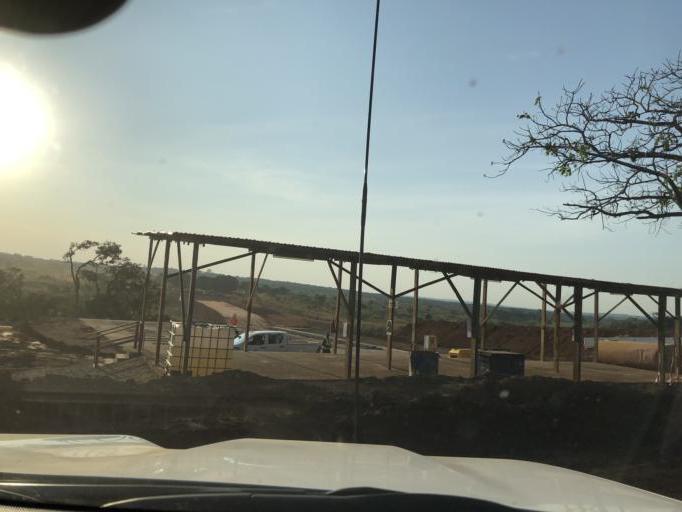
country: CF
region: Nana-Mambere
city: Bouar
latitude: 5.8941
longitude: 15.7614
